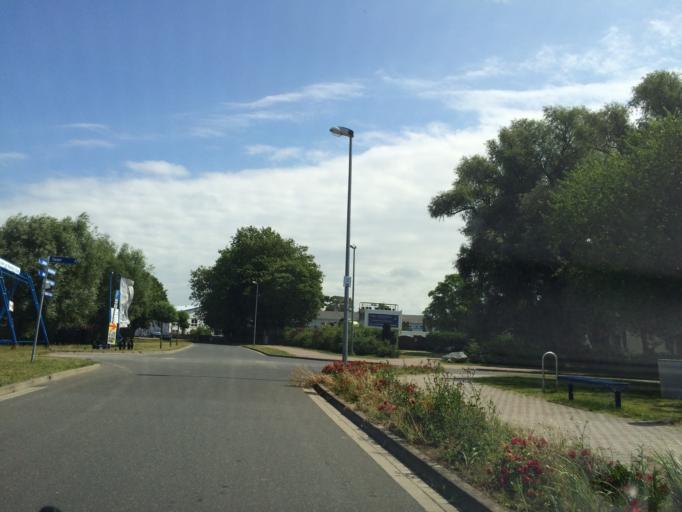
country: DE
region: Mecklenburg-Vorpommern
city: Barth
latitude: 54.3692
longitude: 12.7341
